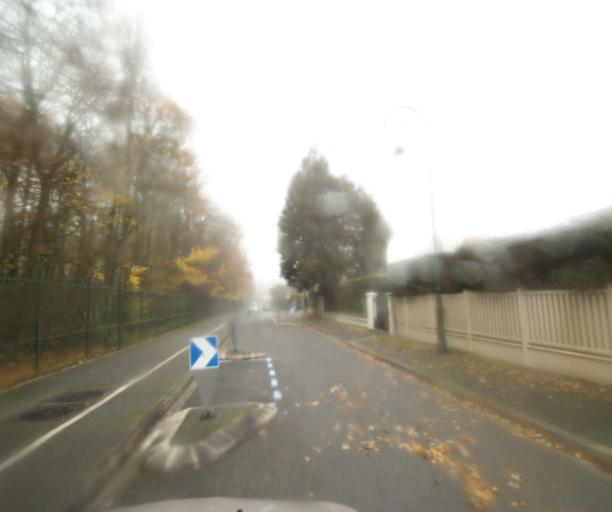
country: FR
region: Ile-de-France
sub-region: Departement de Seine-Saint-Denis
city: Tremblay-en-France
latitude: 48.9399
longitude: 2.5679
